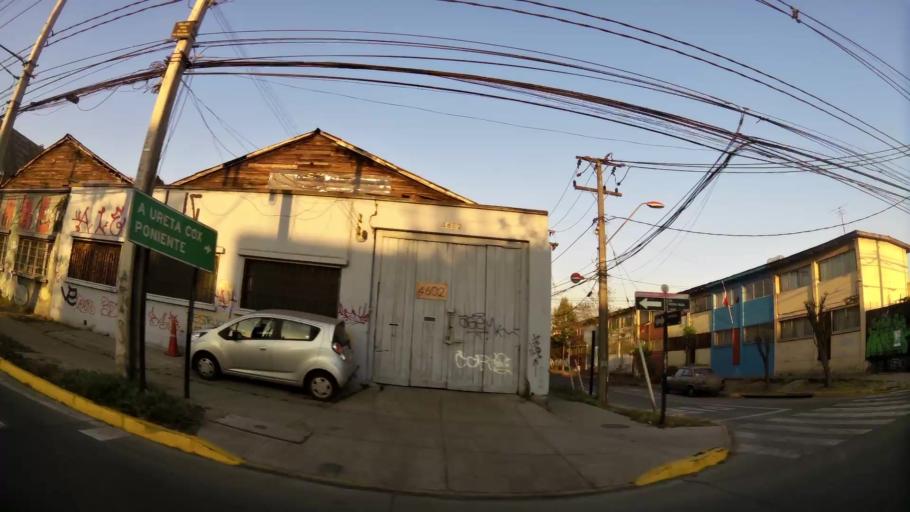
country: CL
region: Santiago Metropolitan
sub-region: Provincia de Santiago
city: Santiago
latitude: -33.4995
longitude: -70.6392
